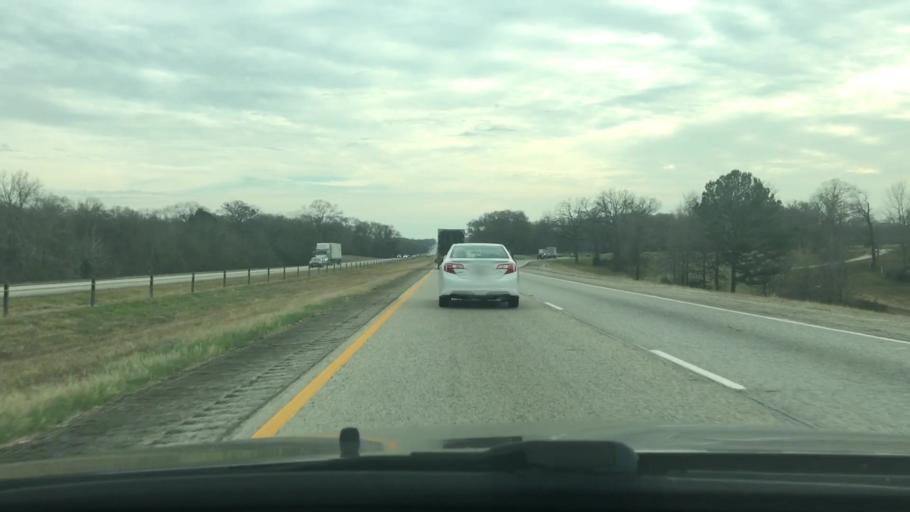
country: US
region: Texas
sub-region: Leon County
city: Centerville
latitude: 31.1982
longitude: -95.9942
